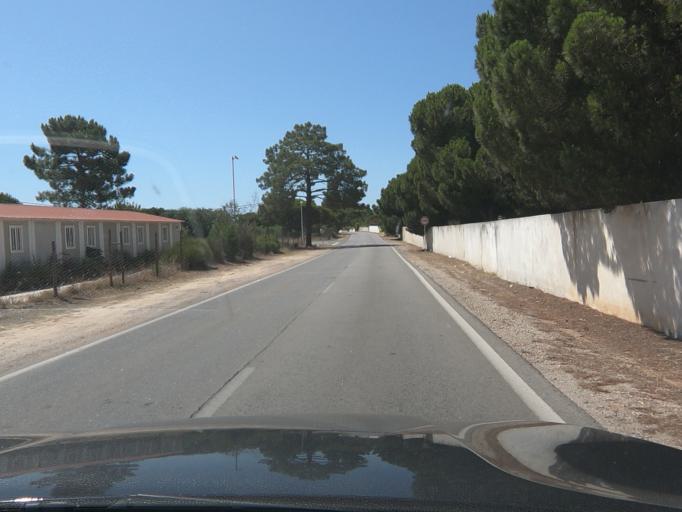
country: PT
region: Faro
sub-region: Loule
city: Vilamoura
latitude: 37.0856
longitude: -8.1009
